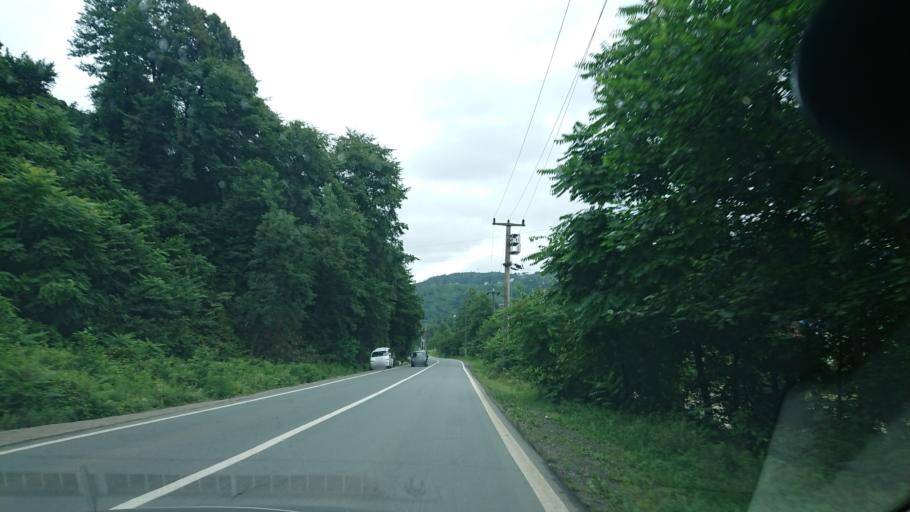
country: TR
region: Rize
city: Gundogdu
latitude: 41.0182
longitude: 40.5717
